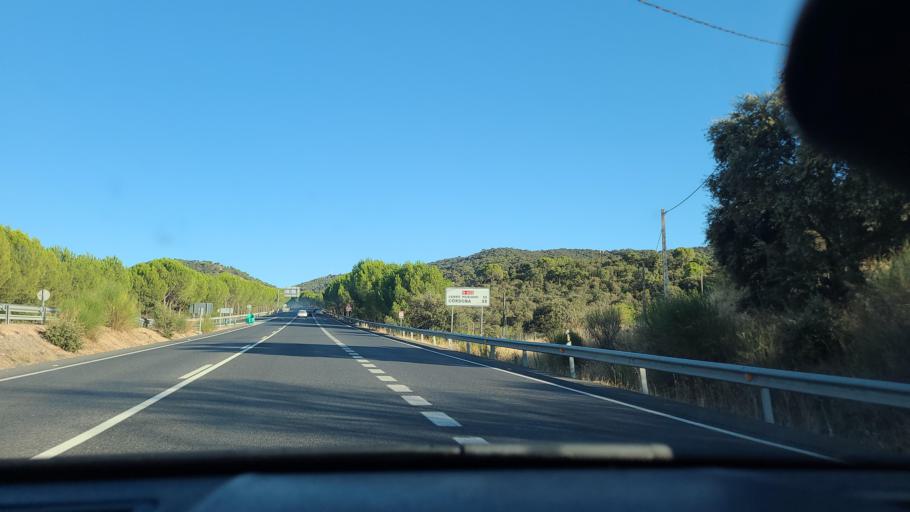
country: ES
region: Andalusia
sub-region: Province of Cordoba
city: Villaharta
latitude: 38.1237
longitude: -4.8989
